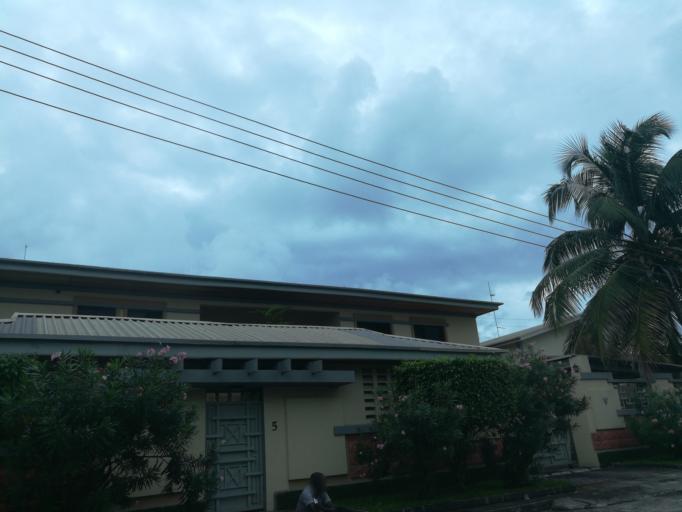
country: NG
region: Lagos
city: Ikoyi
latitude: 6.4460
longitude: 3.4556
